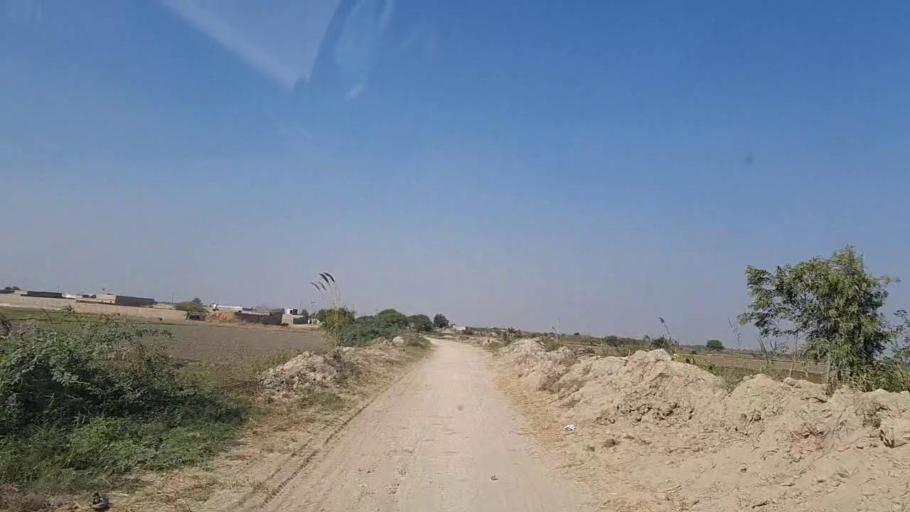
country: PK
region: Sindh
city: Thatta
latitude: 24.7690
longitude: 67.9324
